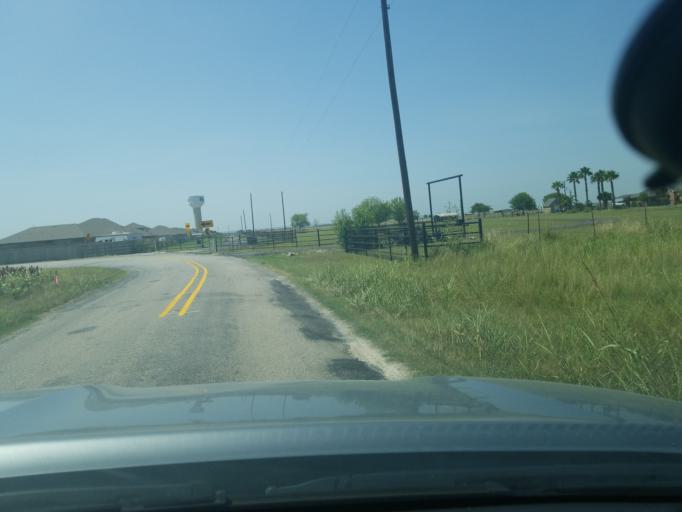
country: US
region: Texas
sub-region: Guadalupe County
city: Lake Dunlap
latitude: 29.6730
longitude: -98.0310
